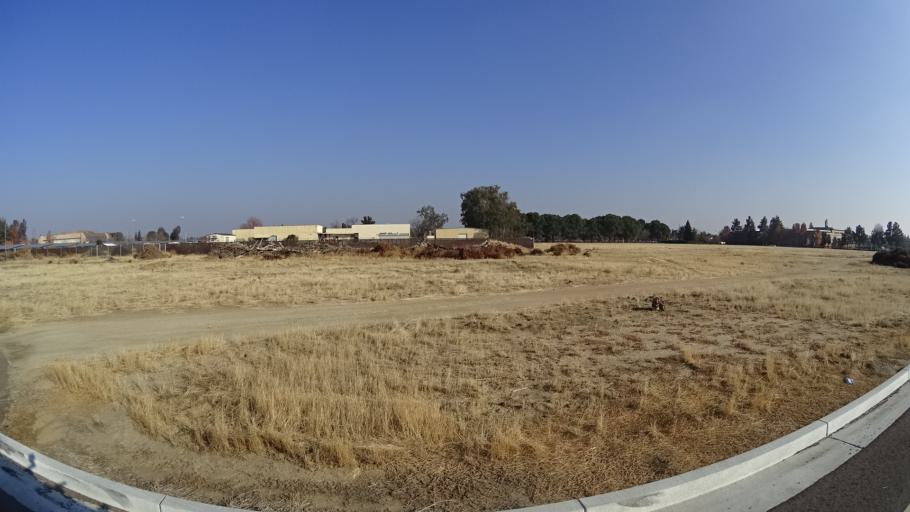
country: US
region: California
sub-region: Kern County
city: Greenacres
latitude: 35.3449
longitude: -119.1061
